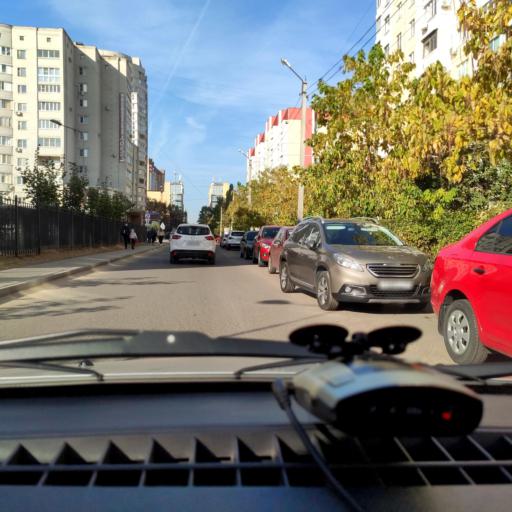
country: RU
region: Voronezj
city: Voronezh
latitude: 51.7103
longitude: 39.1869
